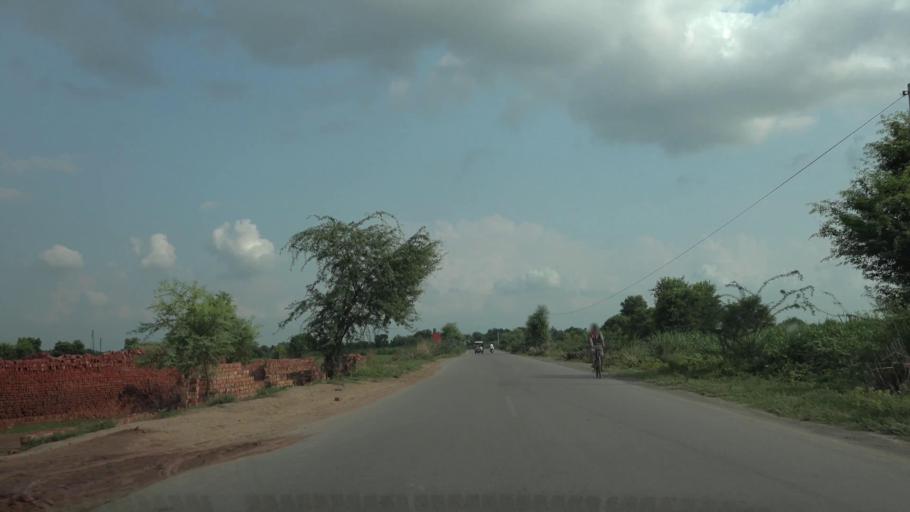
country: PK
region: Punjab
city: Nankana Sahib
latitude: 31.4858
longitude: 73.6096
